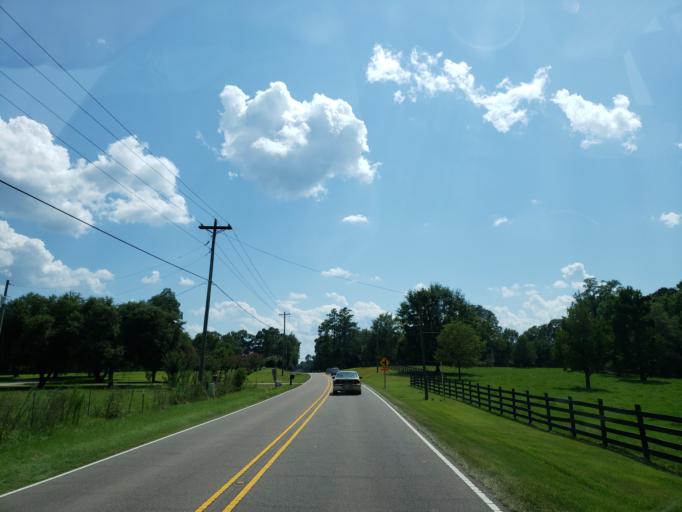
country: US
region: Mississippi
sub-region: Lamar County
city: West Hattiesburg
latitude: 31.2948
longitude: -89.3887
